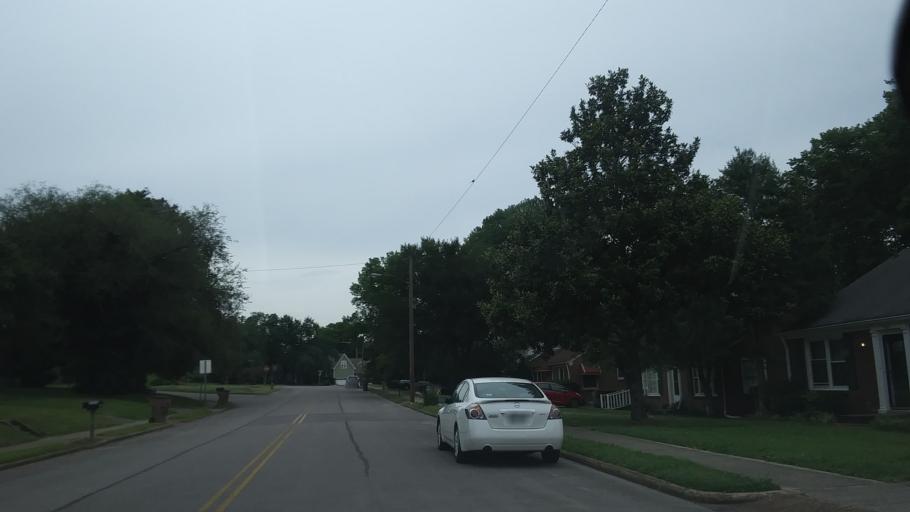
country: US
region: Tennessee
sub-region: Davidson County
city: Belle Meade
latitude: 36.1383
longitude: -86.8546
